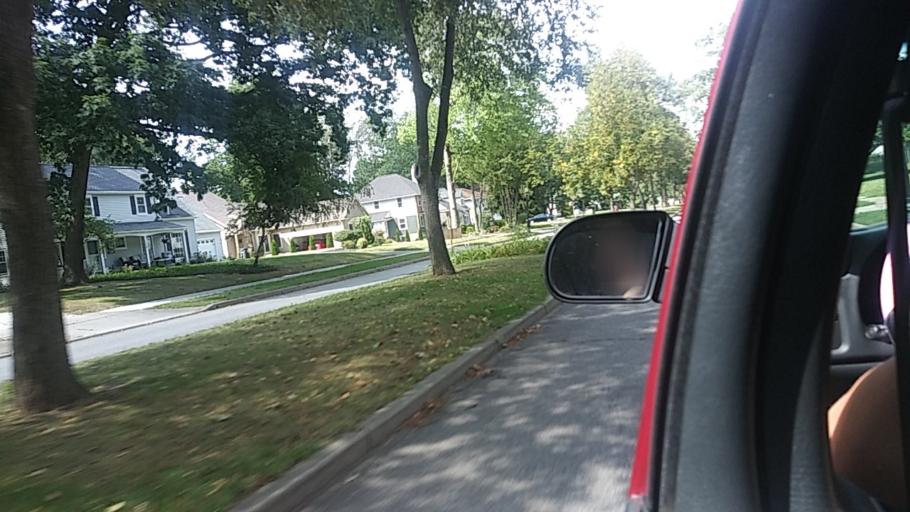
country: US
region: Ohio
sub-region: Summit County
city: Fairlawn
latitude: 41.1141
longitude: -81.5614
